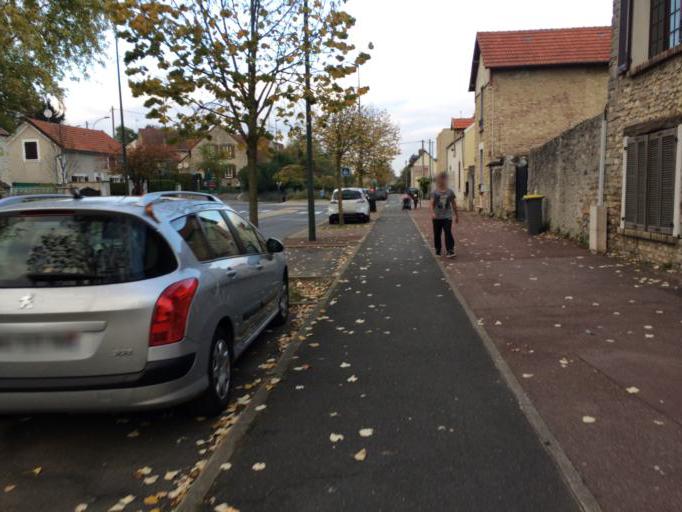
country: FR
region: Ile-de-France
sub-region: Departement de l'Essonne
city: Morigny-Champigny
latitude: 48.4445
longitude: 2.1705
